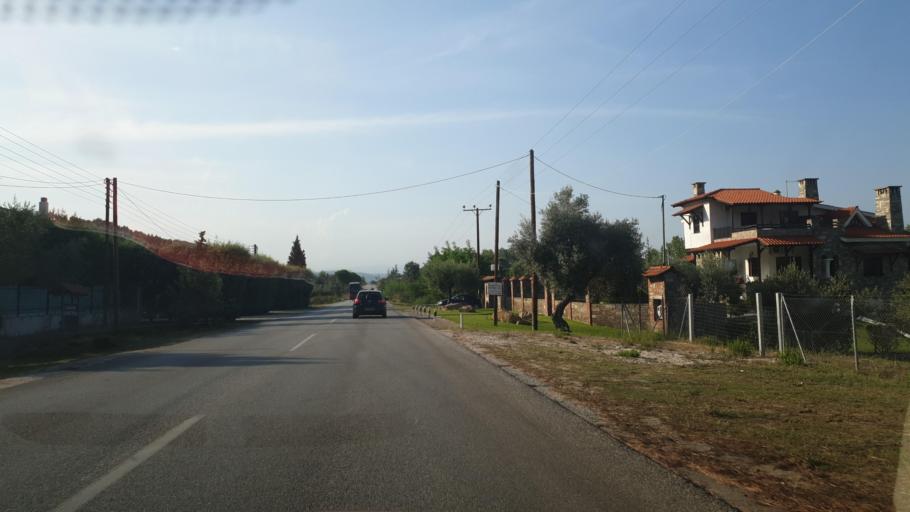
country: GR
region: Central Macedonia
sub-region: Nomos Chalkidikis
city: Agios Nikolaos
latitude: 40.2193
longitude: 23.7498
